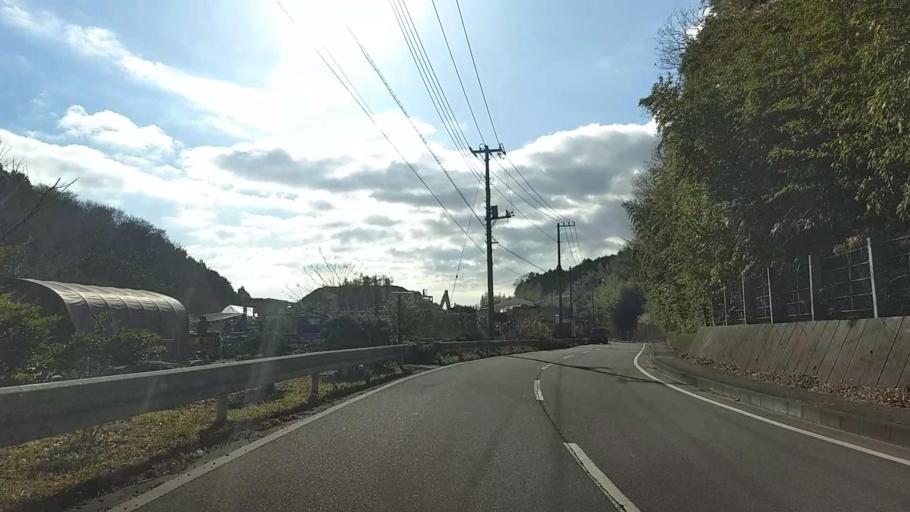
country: JP
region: Kanagawa
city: Isehara
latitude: 35.4585
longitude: 139.2915
